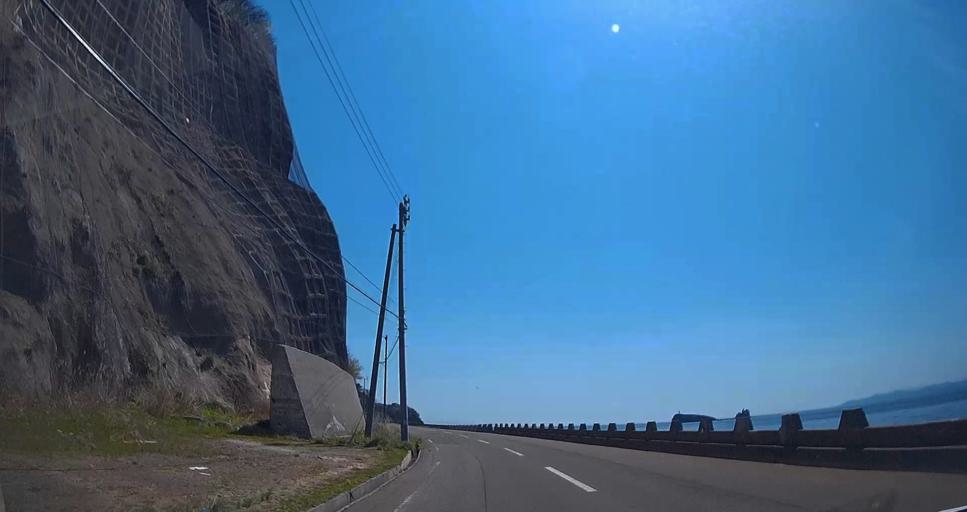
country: JP
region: Aomori
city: Aomori Shi
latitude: 41.1289
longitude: 140.7993
